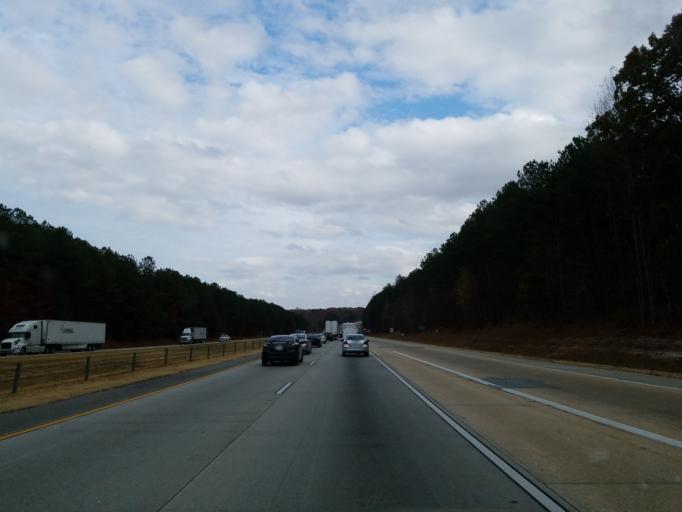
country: US
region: Georgia
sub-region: Haralson County
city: Bremen
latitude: 33.6886
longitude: -85.1838
